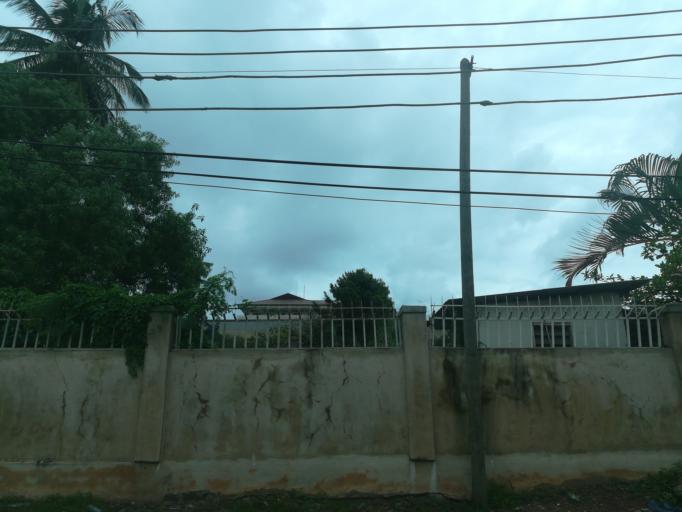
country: NG
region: Lagos
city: Lagos
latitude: 6.4351
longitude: 3.4114
